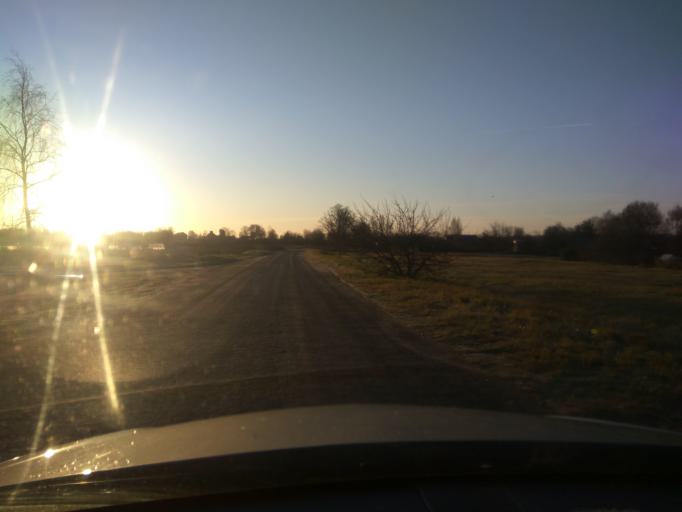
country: LV
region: Kuldigas Rajons
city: Kuldiga
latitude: 56.9651
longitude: 22.0043
